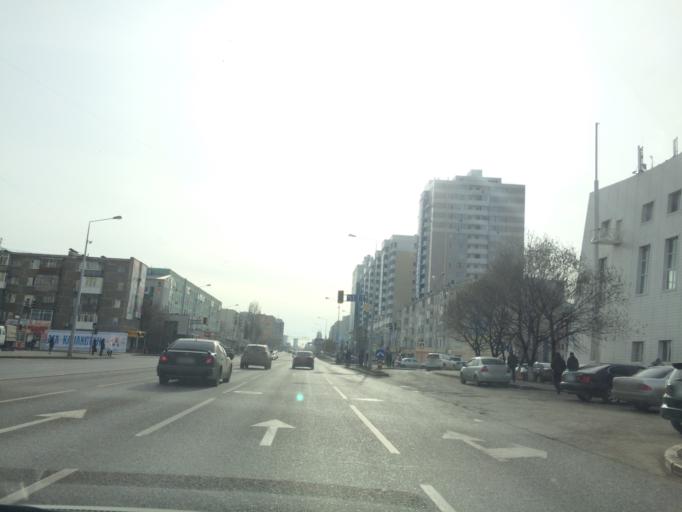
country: KZ
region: Astana Qalasy
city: Astana
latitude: 51.1700
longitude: 71.4077
